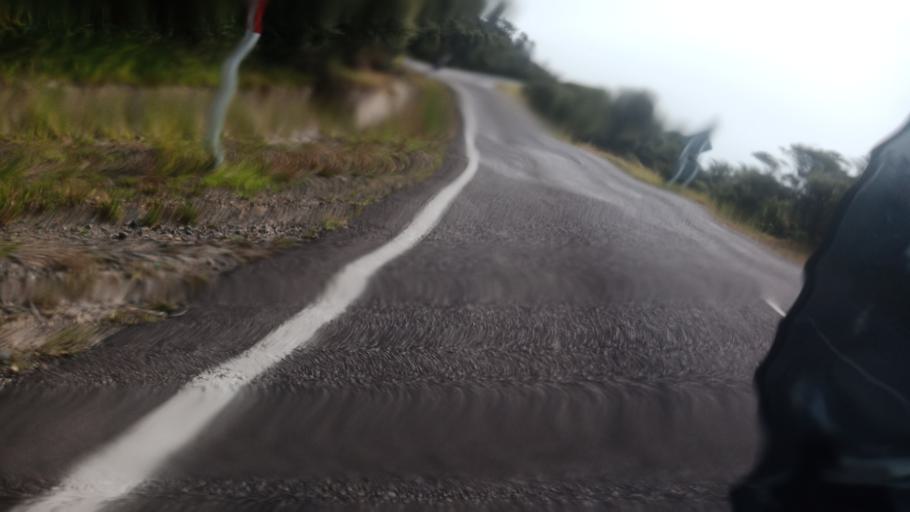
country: NZ
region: Bay of Plenty
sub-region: Opotiki District
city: Opotiki
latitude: -37.6671
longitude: 177.8092
